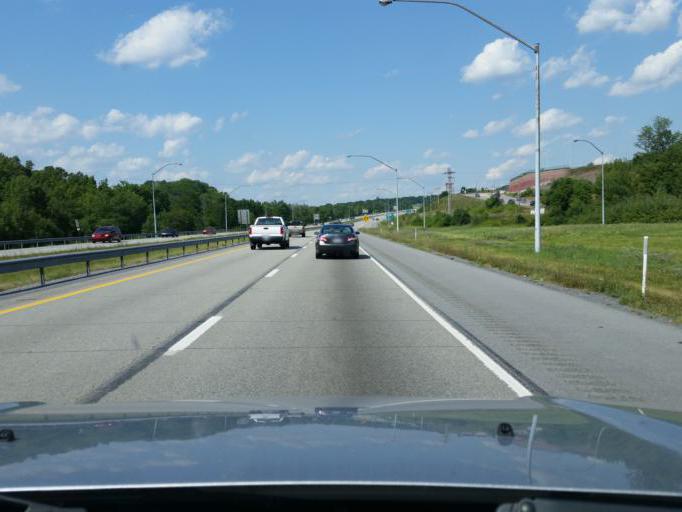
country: US
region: Pennsylvania
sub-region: Blair County
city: Lakemont
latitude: 40.4813
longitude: -78.3930
